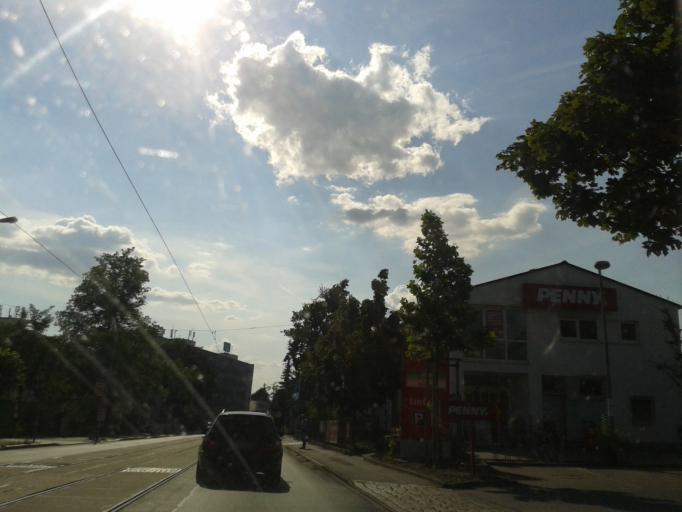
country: DE
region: Saxony
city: Radebeul
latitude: 51.1038
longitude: 13.6728
